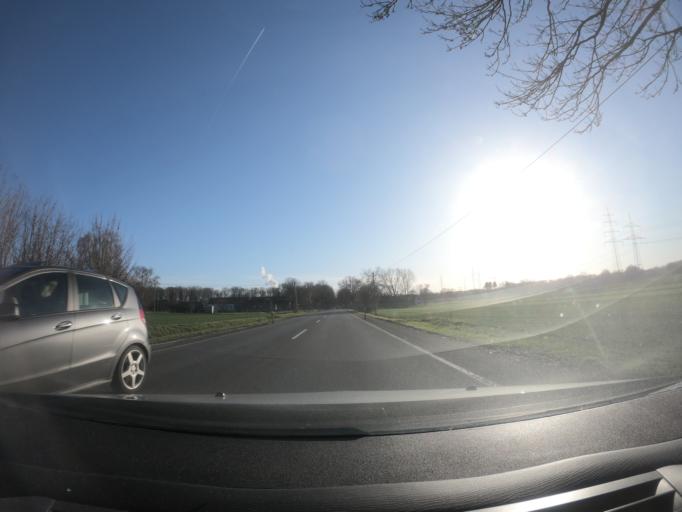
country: DE
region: North Rhine-Westphalia
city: Waltrop
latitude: 51.6316
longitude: 7.4413
